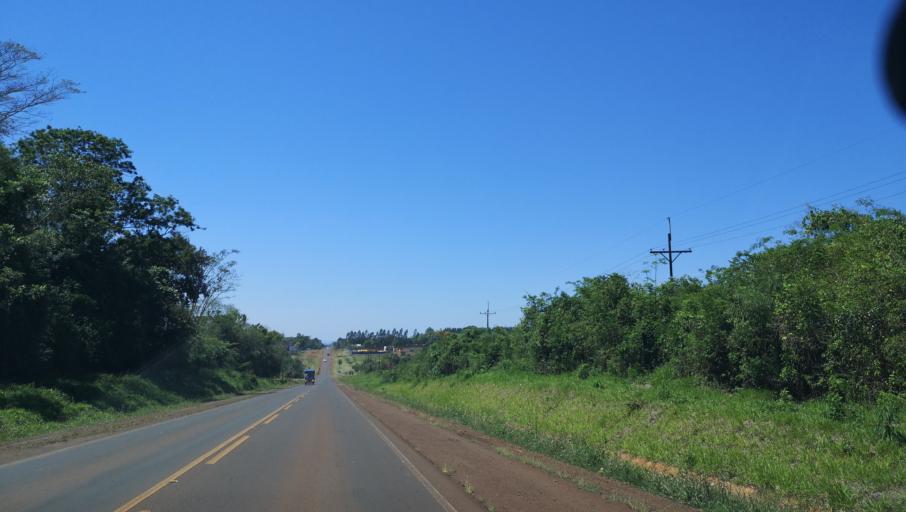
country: PY
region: Itapua
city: San Juan del Parana
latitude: -27.2685
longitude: -55.9575
